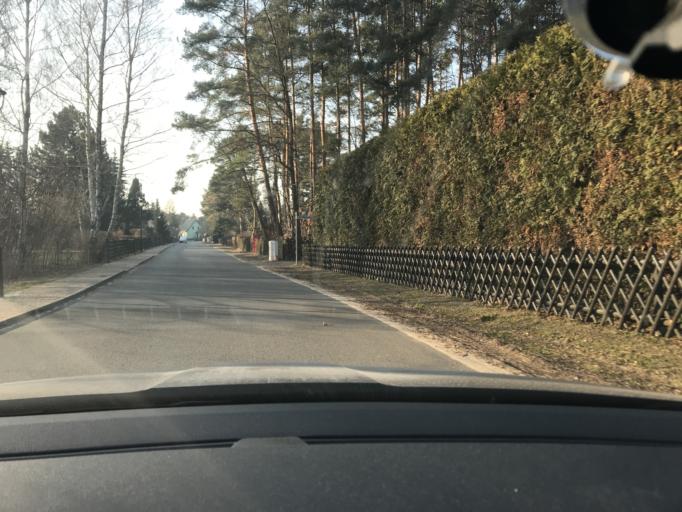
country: DE
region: Brandenburg
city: Munchehofe
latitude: 52.2179
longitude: 13.7790
